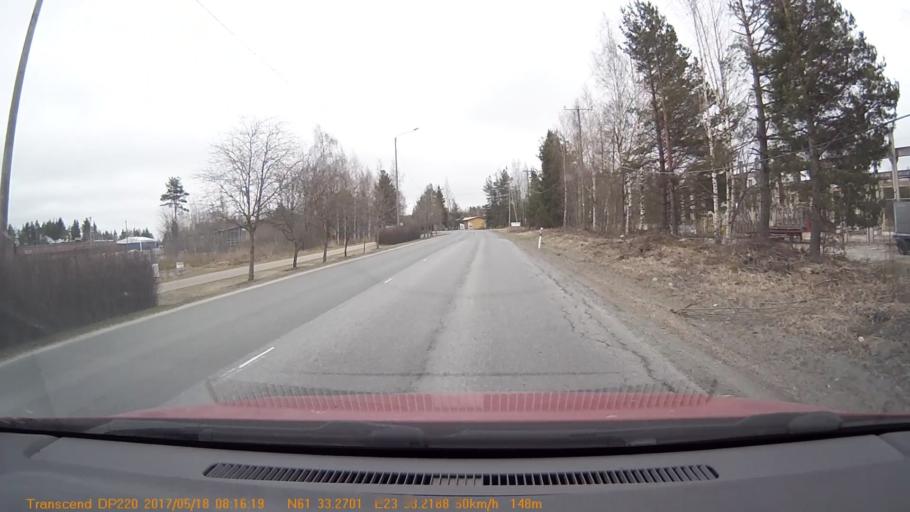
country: FI
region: Pirkanmaa
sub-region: Tampere
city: Yloejaervi
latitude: 61.5545
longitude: 23.5537
